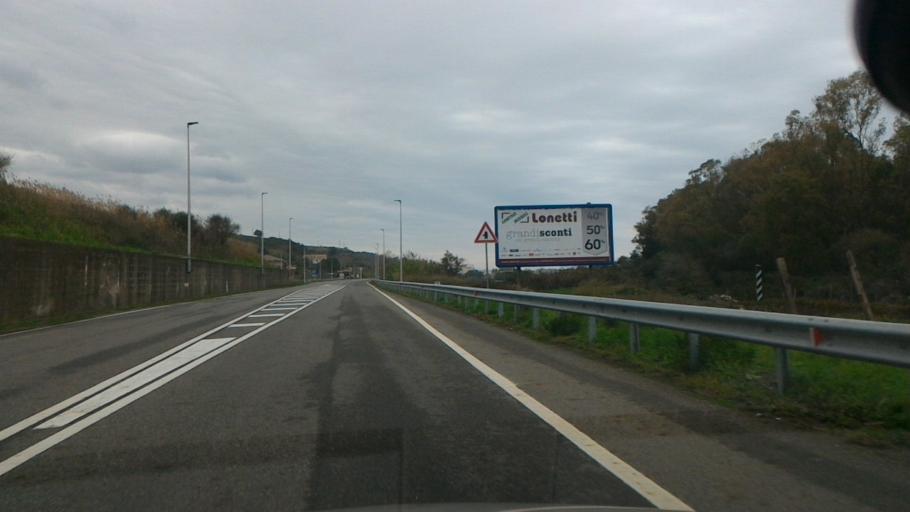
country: IT
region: Calabria
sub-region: Provincia di Crotone
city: Torretta
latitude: 39.4331
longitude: 17.0583
